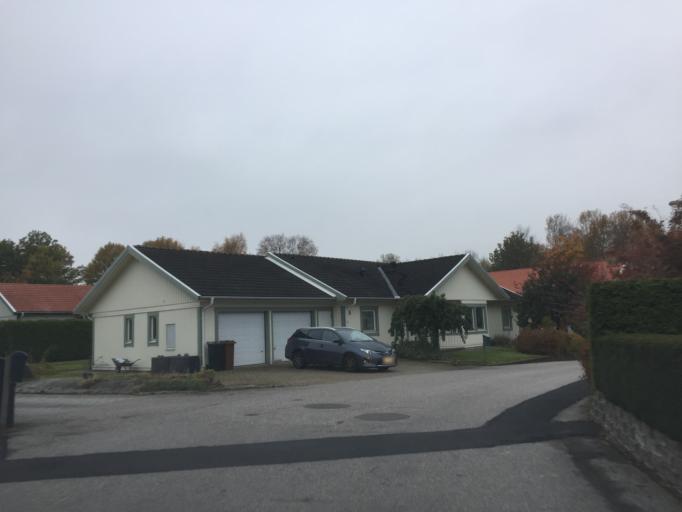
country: SE
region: Vaestra Goetaland
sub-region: Trollhattan
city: Trollhattan
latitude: 58.2796
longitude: 12.3283
